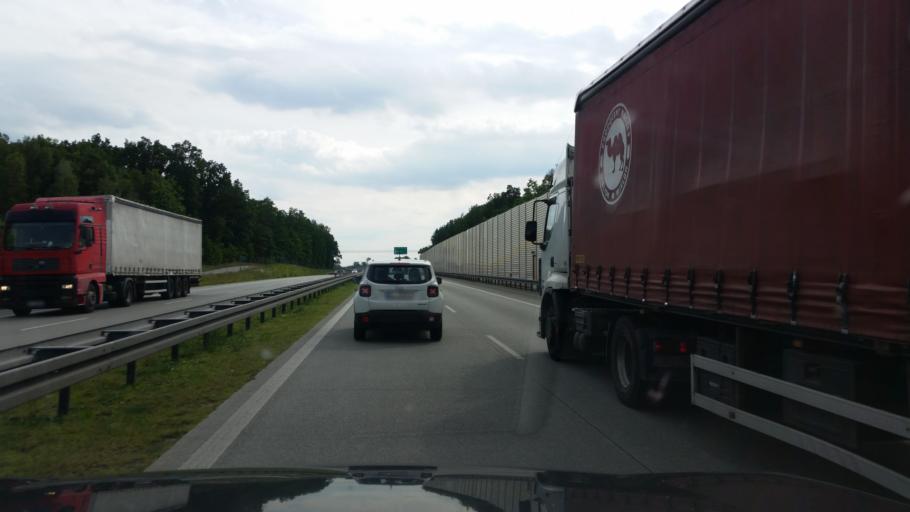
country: PL
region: Lodz Voivodeship
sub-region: Powiat rawski
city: Rawa Mazowiecka
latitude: 51.8121
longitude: 20.3096
